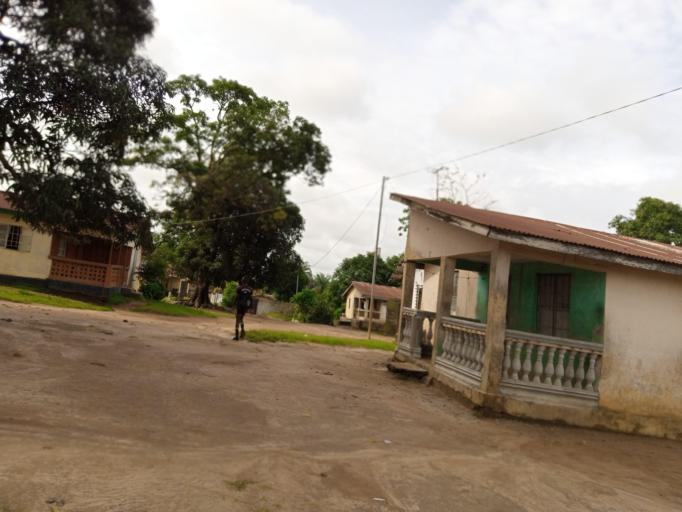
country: SL
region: Northern Province
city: Masoyila
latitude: 8.6012
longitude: -13.2015
